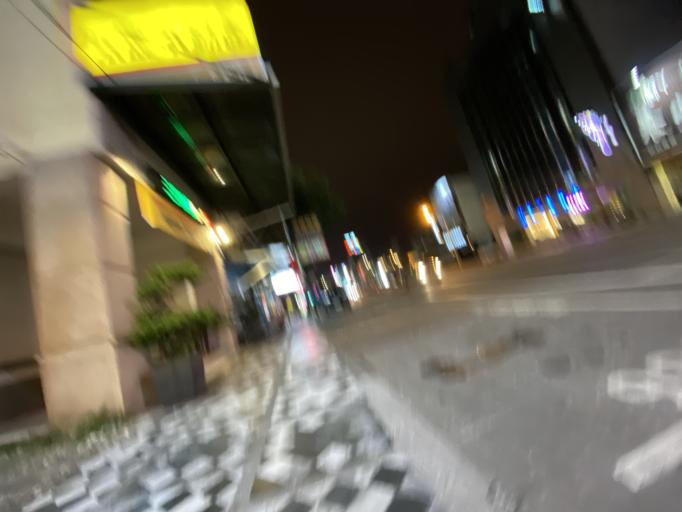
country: TW
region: Taiwan
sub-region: Hualien
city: Hualian
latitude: 23.9886
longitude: 121.6003
